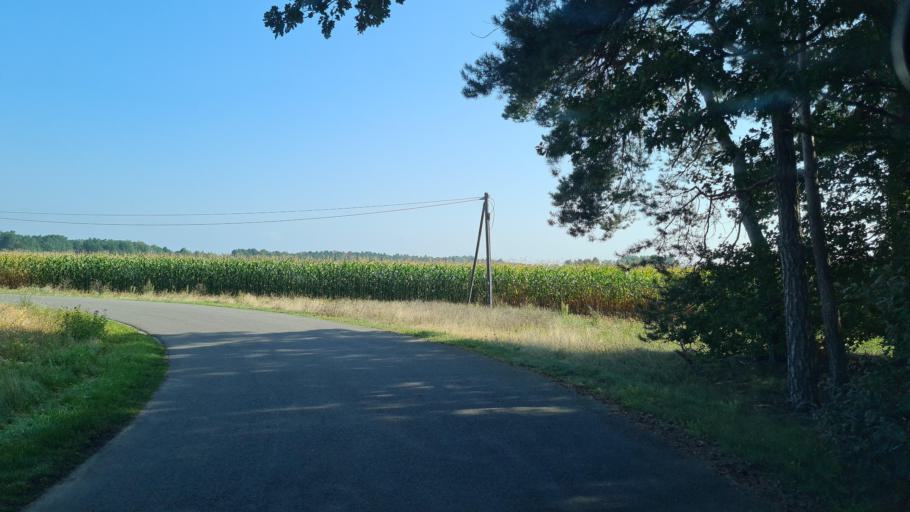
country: DE
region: Brandenburg
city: Luckau
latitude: 51.7752
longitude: 13.7014
